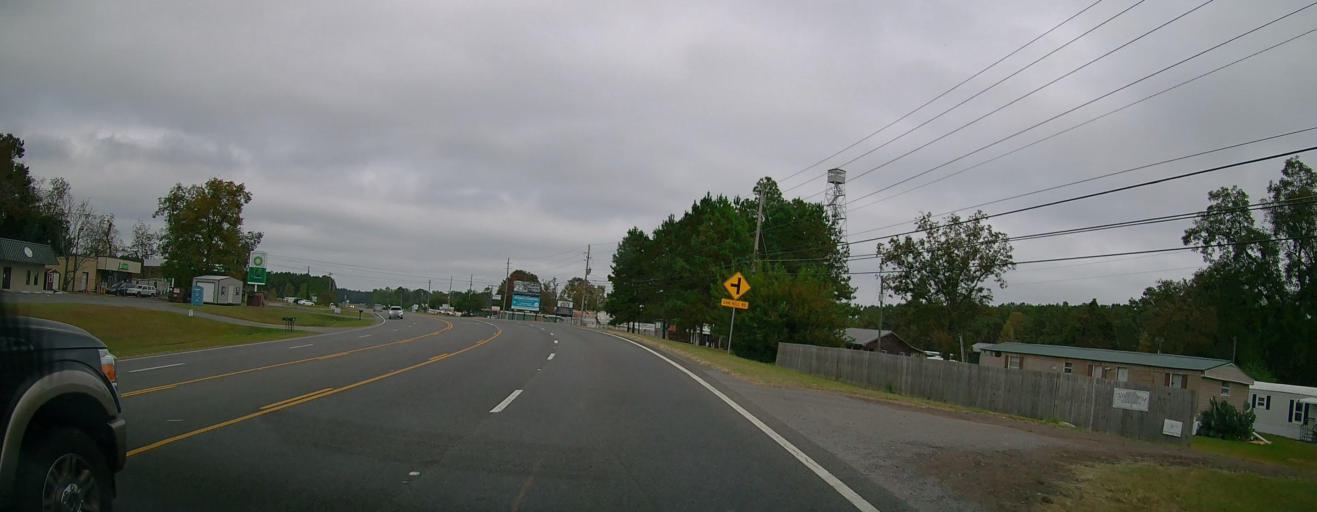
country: US
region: Georgia
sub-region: Thomas County
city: Thomasville
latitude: 30.8799
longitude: -83.9316
